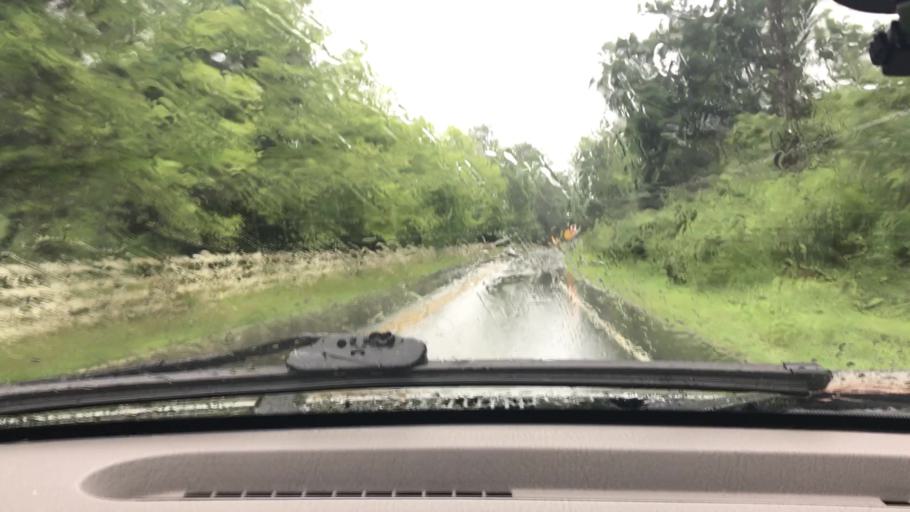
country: US
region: Pennsylvania
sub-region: Lancaster County
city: Elizabethtown
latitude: 40.1571
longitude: -76.6262
